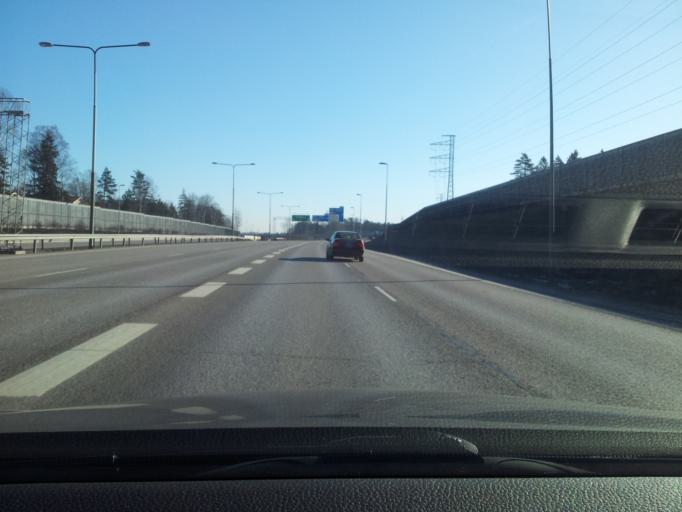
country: FI
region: Uusimaa
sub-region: Helsinki
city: Kilo
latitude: 60.2081
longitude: 24.8037
